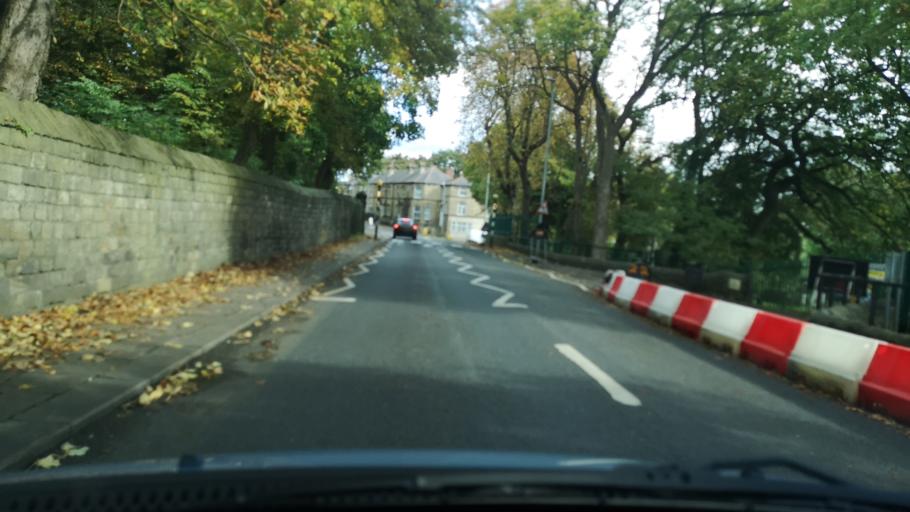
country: GB
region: England
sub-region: Kirklees
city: Dewsbury
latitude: 53.6871
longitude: -1.6458
